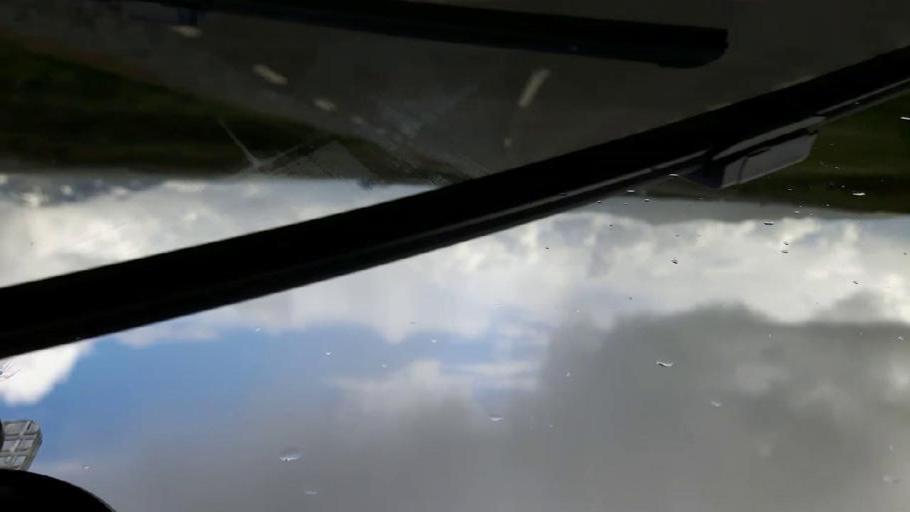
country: NO
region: Nordland
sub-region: Hattfjelldal
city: Hattfjelldal
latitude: 65.1033
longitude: 14.4698
